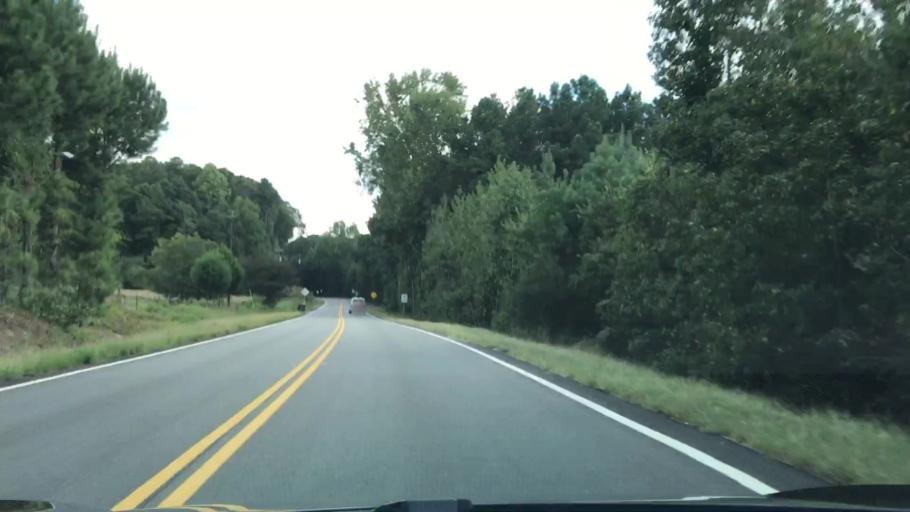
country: US
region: Georgia
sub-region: Greene County
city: Union Point
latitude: 33.5419
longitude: -83.0938
